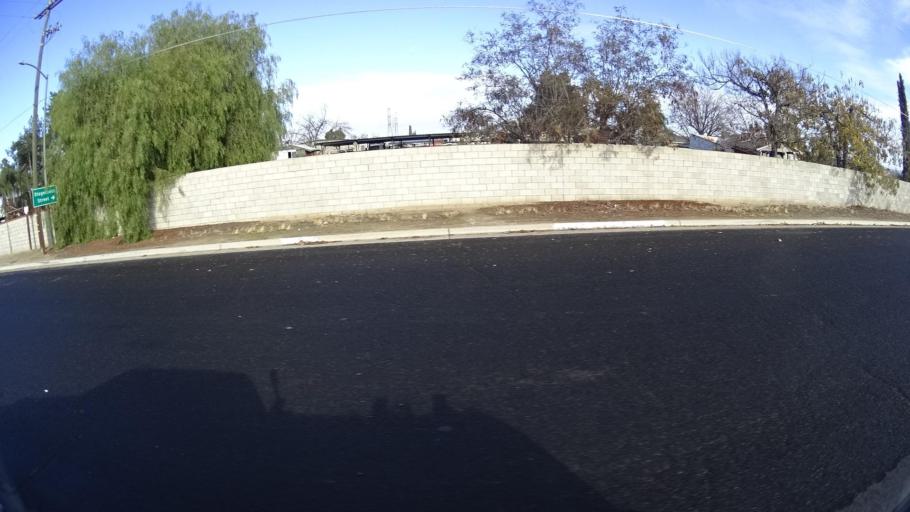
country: US
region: California
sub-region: Kern County
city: Rosedale
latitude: 35.3835
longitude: -119.2008
